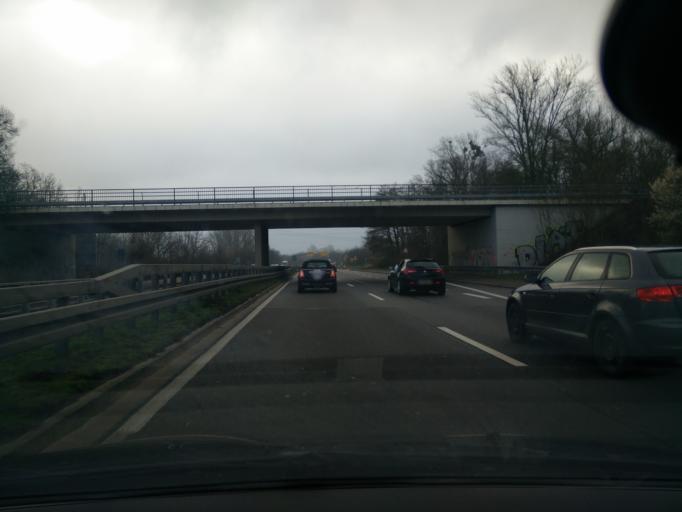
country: DE
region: Rheinland-Pfalz
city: Worth am Rhein
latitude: 49.0373
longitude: 8.3189
